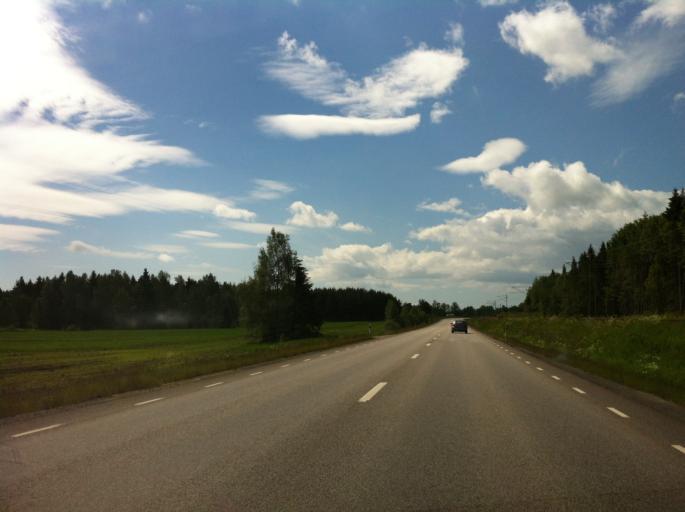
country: SE
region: Vaermland
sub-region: Saffle Kommun
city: Saeffle
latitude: 59.1694
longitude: 13.0018
